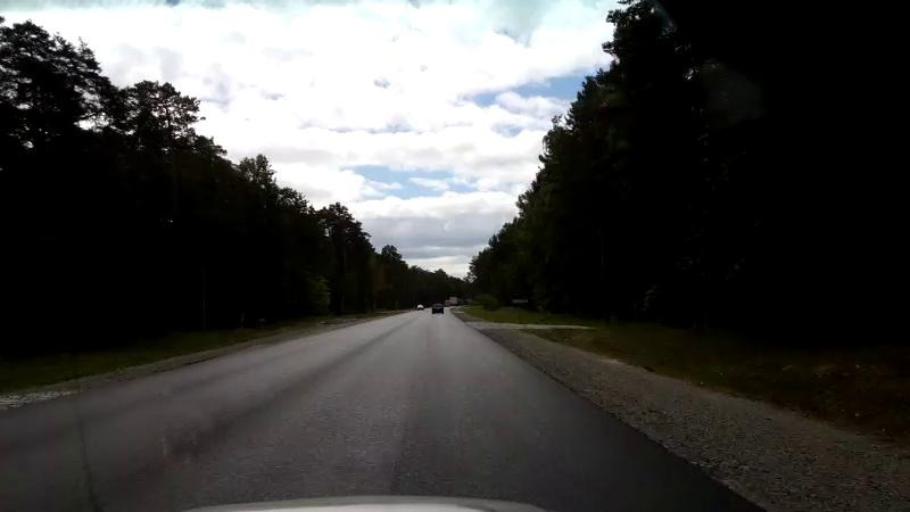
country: LV
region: Salacgrivas
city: Ainazi
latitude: 57.8186
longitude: 24.3470
